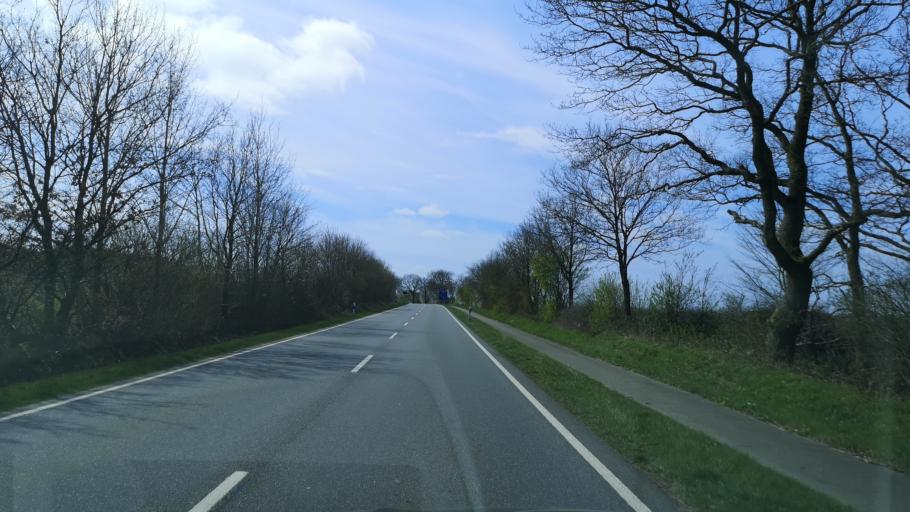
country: DE
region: Schleswig-Holstein
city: Albersdorf
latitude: 54.1223
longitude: 9.2679
